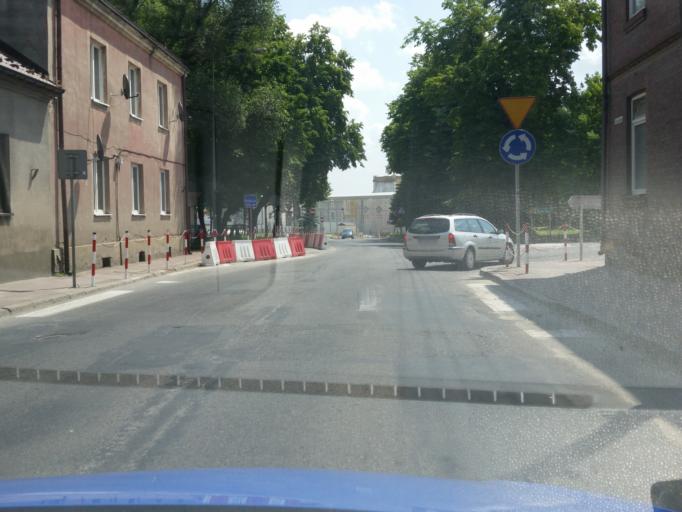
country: PL
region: Swietokrzyskie
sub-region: Powiat kazimierski
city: Kazimierza Wielka
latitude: 50.2675
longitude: 20.4897
